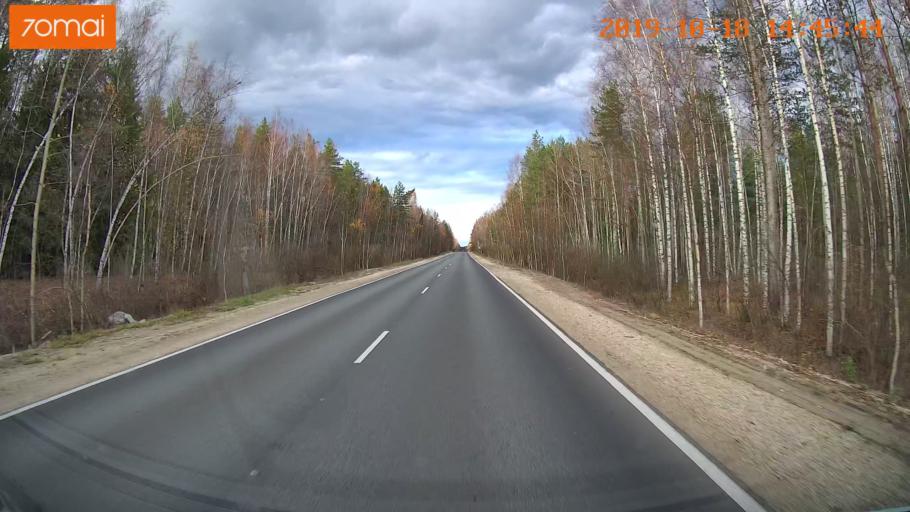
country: RU
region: Vladimir
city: Velikodvorskiy
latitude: 55.3597
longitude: 40.6795
